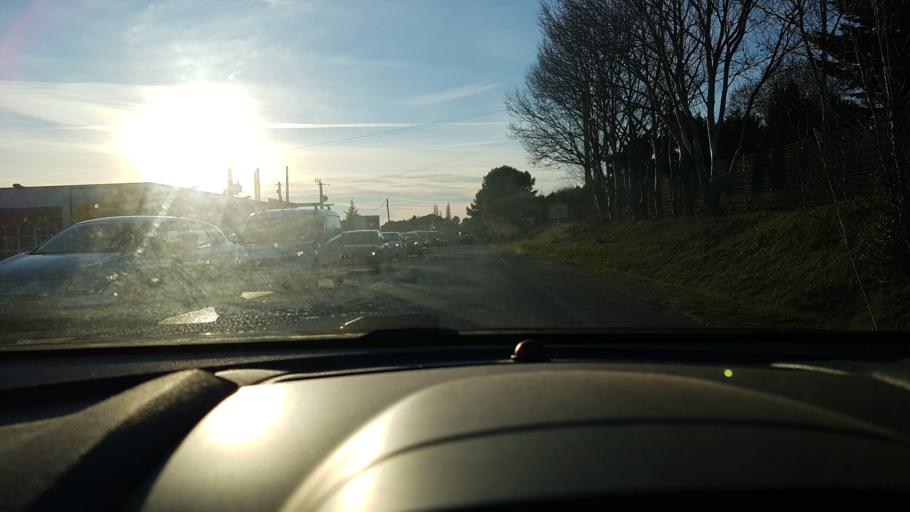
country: FR
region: Provence-Alpes-Cote d'Azur
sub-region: Departement des Bouches-du-Rhone
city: Simiane-Collongue
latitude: 43.4493
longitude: 5.4468
